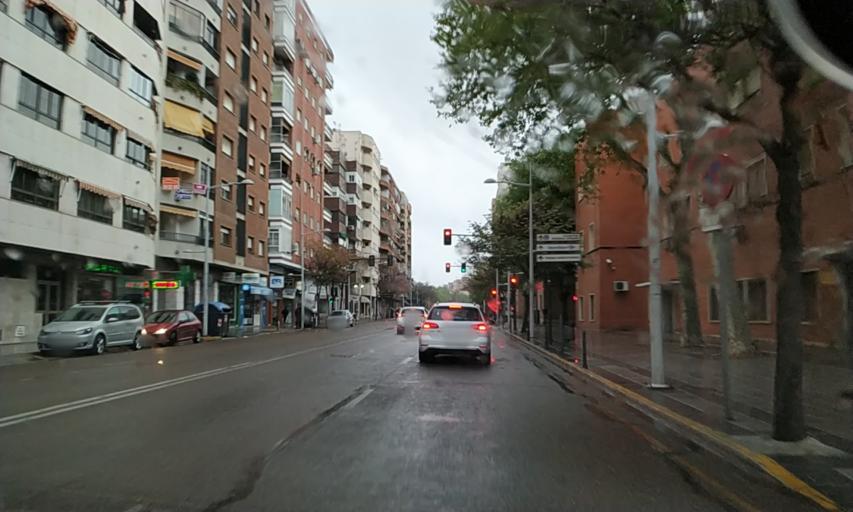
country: ES
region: Extremadura
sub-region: Provincia de Badajoz
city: Badajoz
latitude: 38.8716
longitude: -6.9730
